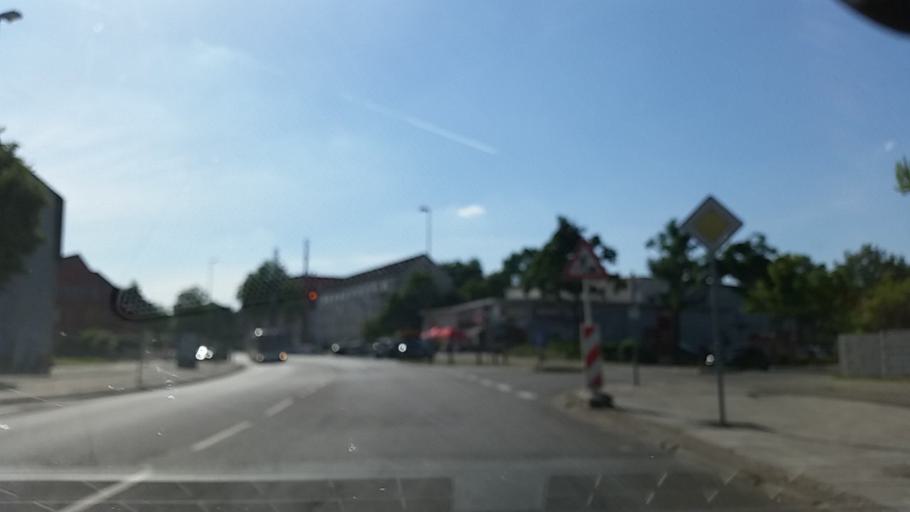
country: DE
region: Lower Saxony
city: Wolfsburg
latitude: 52.4211
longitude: 10.7669
